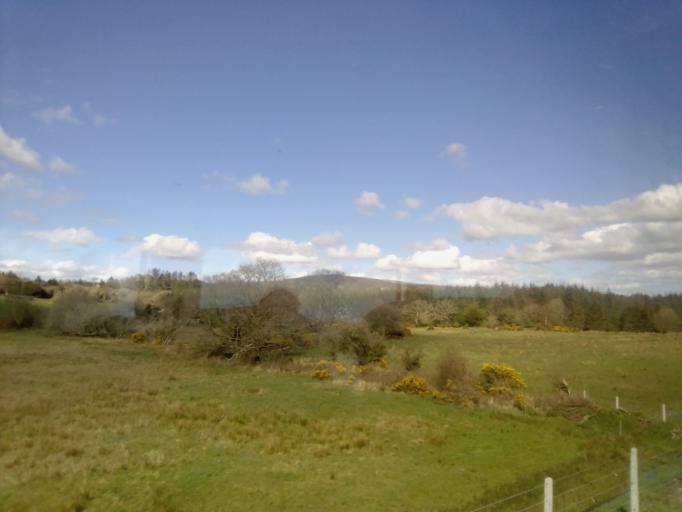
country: IE
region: Munster
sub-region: Ciarrai
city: Cill Airne
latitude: 52.0356
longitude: -9.4450
